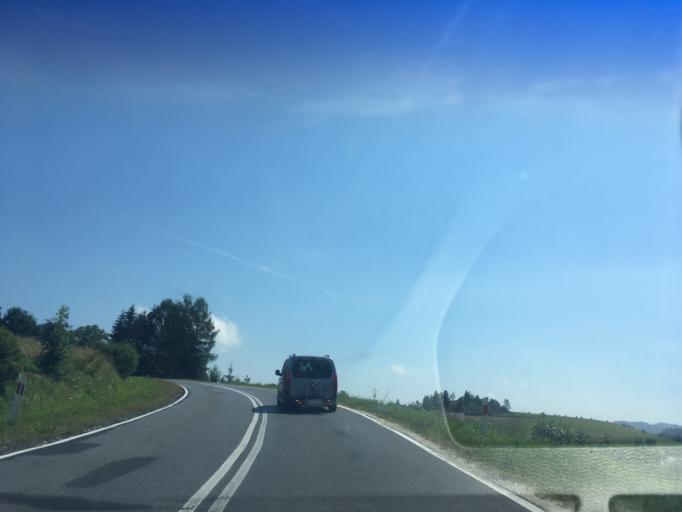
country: PL
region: Lesser Poland Voivodeship
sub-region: Powiat nowotarski
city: Krosnica
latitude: 49.4079
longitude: 20.3480
